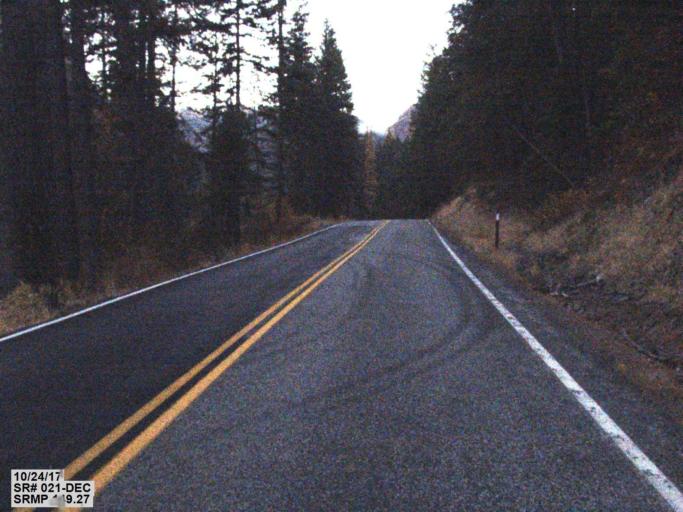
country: US
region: Washington
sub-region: Ferry County
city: Republic
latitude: 48.4949
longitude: -118.7408
